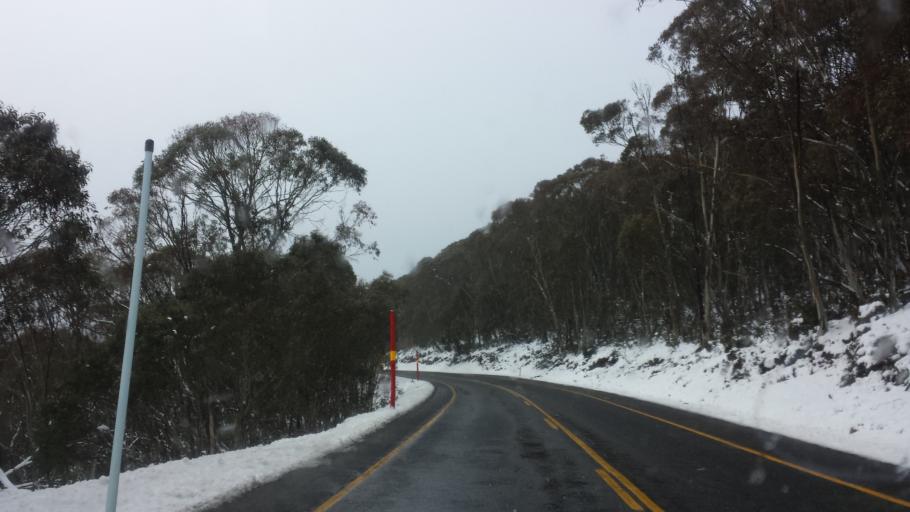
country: AU
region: Victoria
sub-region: Alpine
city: Mount Beauty
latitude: -37.0225
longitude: 147.2653
